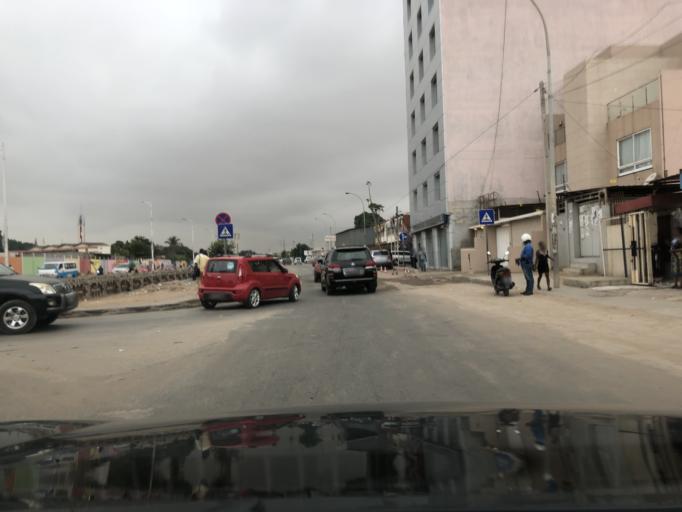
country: AO
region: Luanda
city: Luanda
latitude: -8.8280
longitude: 13.2541
